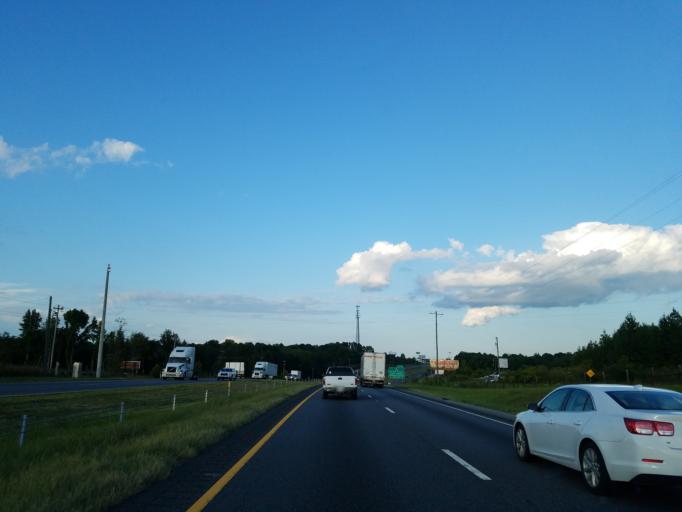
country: US
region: South Carolina
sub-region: Cherokee County
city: Gaffney
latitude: 35.0944
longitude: -81.6847
